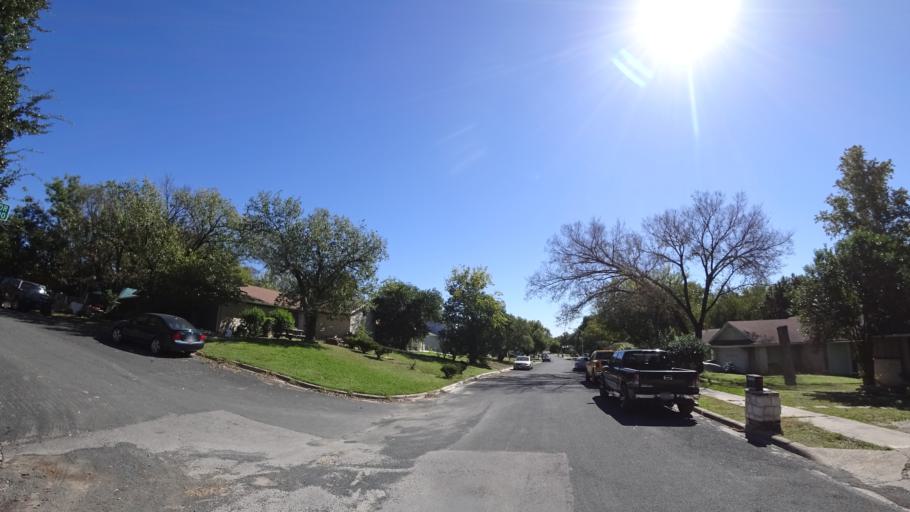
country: US
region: Texas
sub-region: Travis County
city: Austin
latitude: 30.2888
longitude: -97.6620
